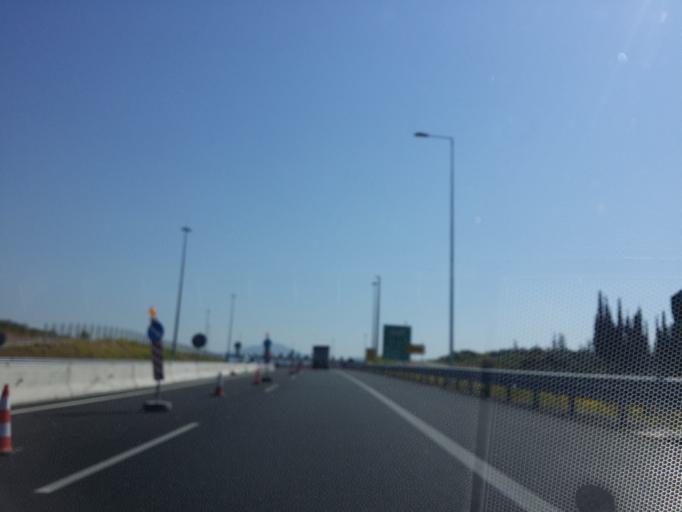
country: GR
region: Peloponnese
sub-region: Nomos Korinthias
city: Moulki
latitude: 38.0005
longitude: 22.7355
